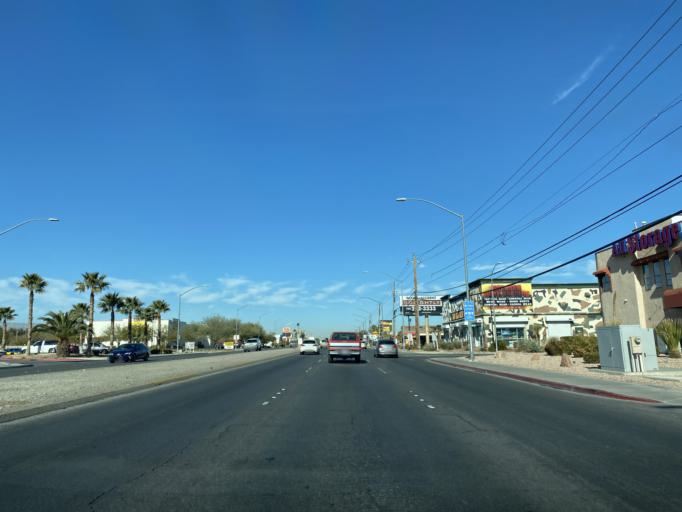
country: US
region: Nevada
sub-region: Clark County
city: Las Vegas
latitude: 36.2185
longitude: -115.2132
